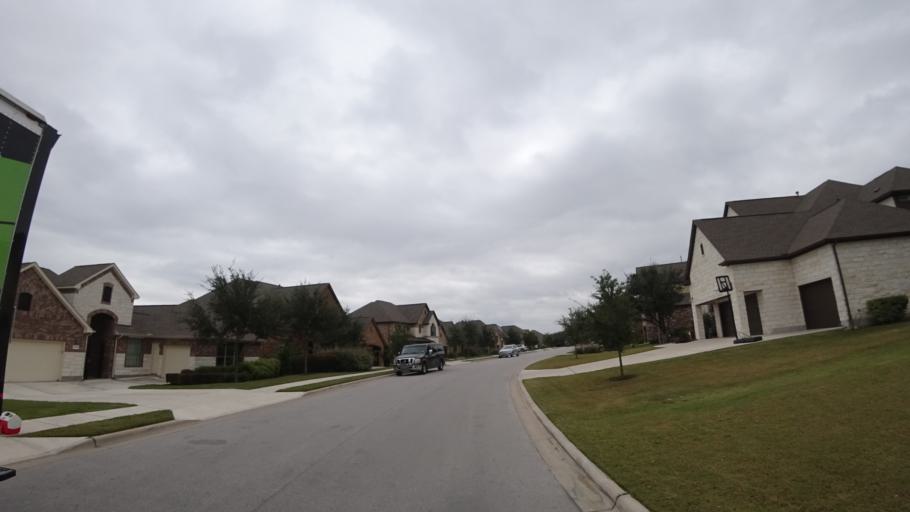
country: US
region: Texas
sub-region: Travis County
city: Bee Cave
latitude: 30.3445
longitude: -97.9053
